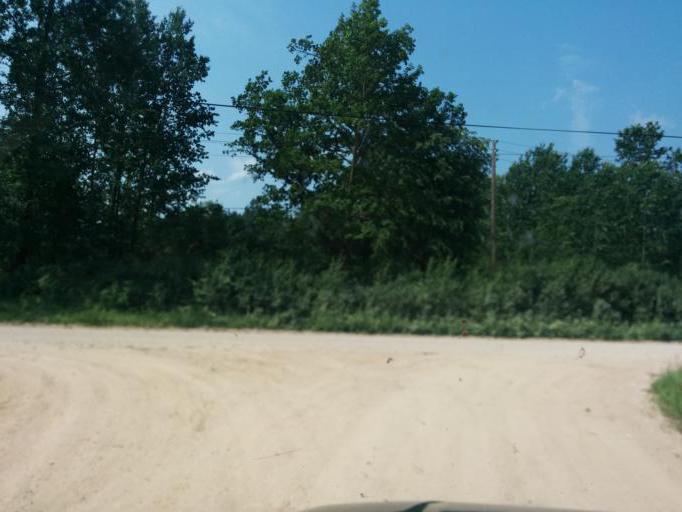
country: LV
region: Baldone
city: Baldone
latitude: 56.7432
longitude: 24.4784
